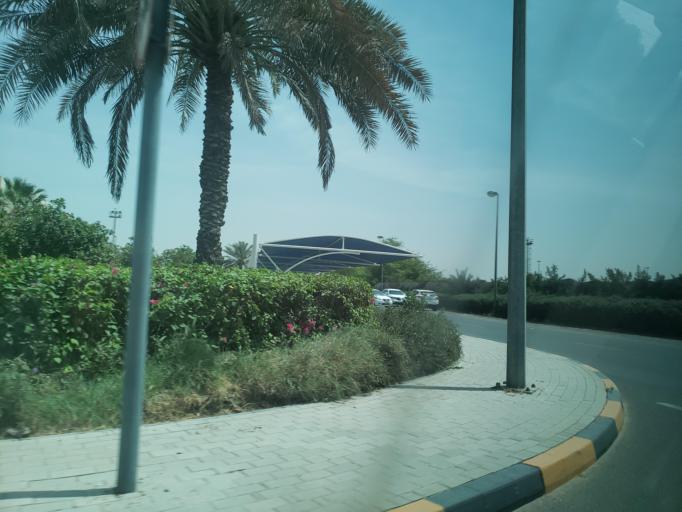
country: AE
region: Ash Shariqah
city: Sharjah
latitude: 25.3294
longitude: 55.4993
